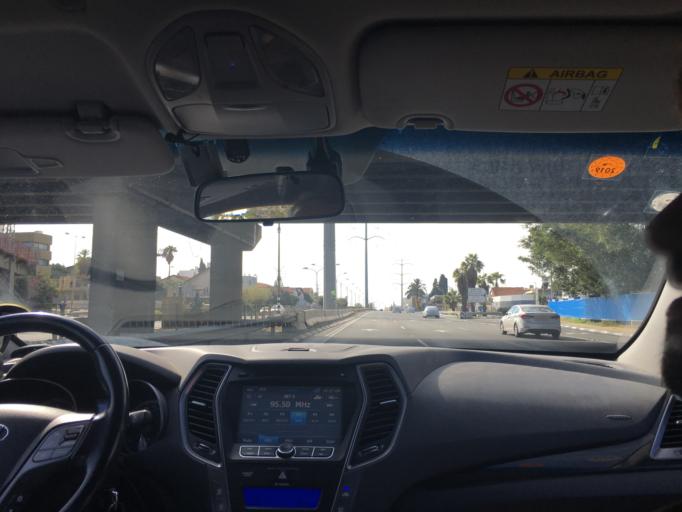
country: IL
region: Tel Aviv
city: Giv`at Shemu'el
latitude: 32.0768
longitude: 34.8441
